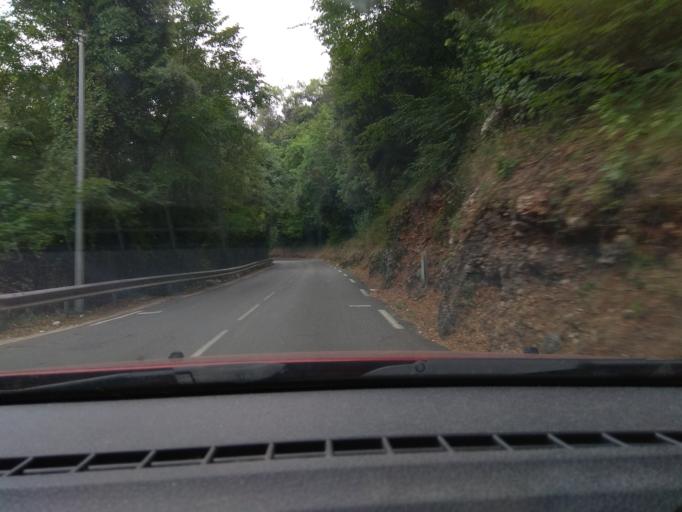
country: FR
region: Provence-Alpes-Cote d'Azur
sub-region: Departement des Alpes-Maritimes
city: La Colle-sur-Loup
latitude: 43.6816
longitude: 7.0769
